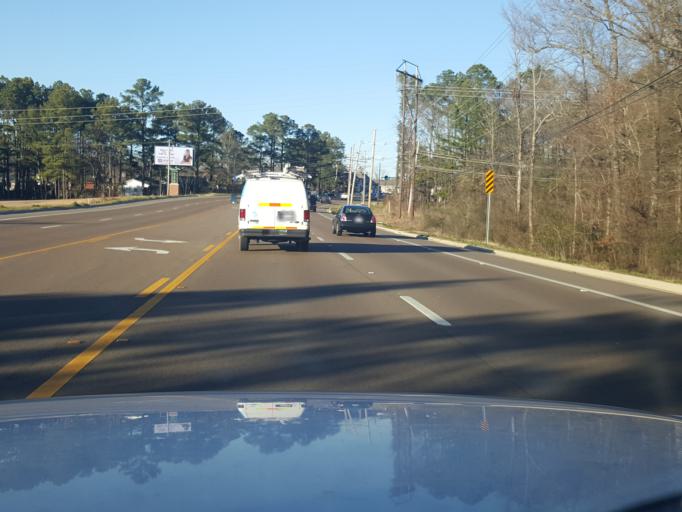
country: US
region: Mississippi
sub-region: Rankin County
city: Flowood
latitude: 32.3547
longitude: -90.0618
